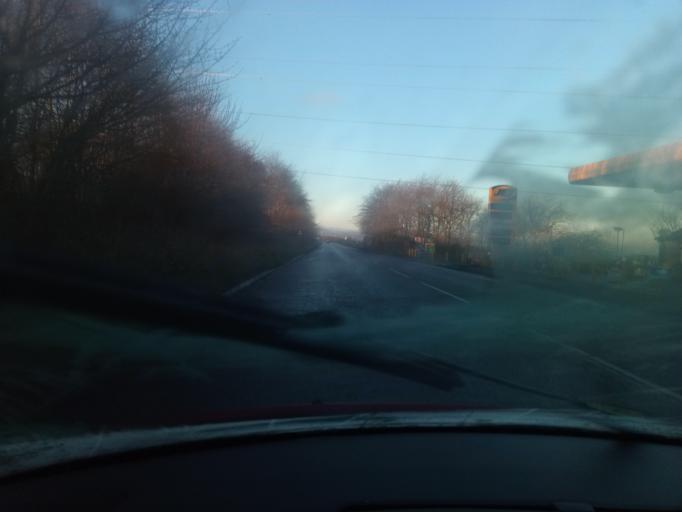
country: GB
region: Scotland
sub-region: East Lothian
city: Tranent
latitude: 55.9464
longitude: -2.9694
